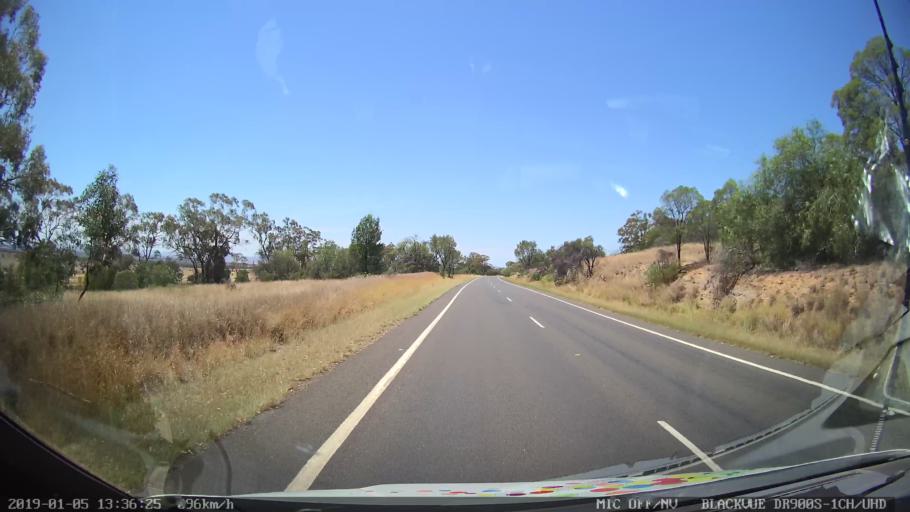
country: AU
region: New South Wales
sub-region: Gunnedah
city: Gunnedah
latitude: -30.9851
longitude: 150.1643
